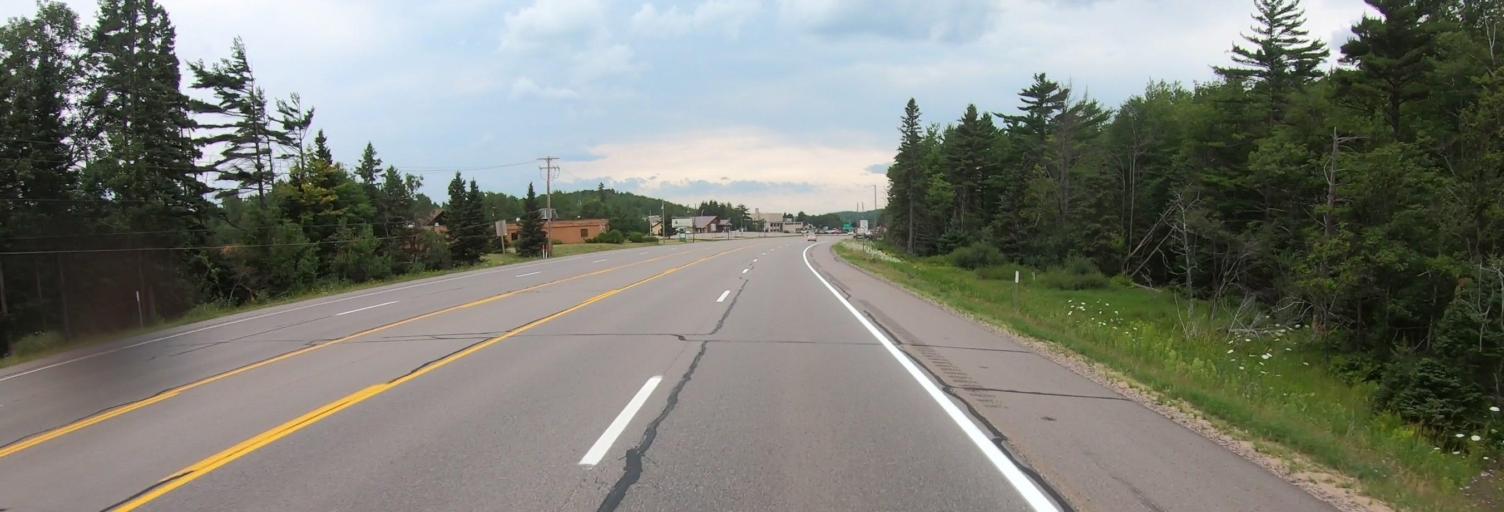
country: US
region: Michigan
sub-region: Marquette County
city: Ishpeming
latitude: 46.5083
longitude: -87.6485
